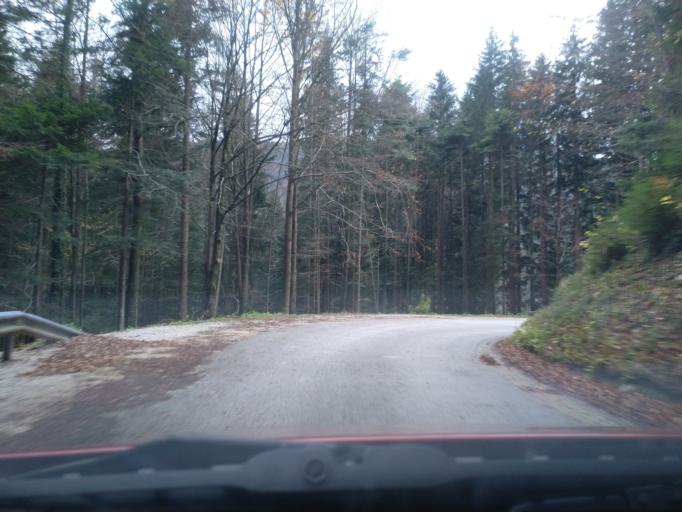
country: SI
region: Luce
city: Luce
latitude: 46.3040
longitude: 14.7032
